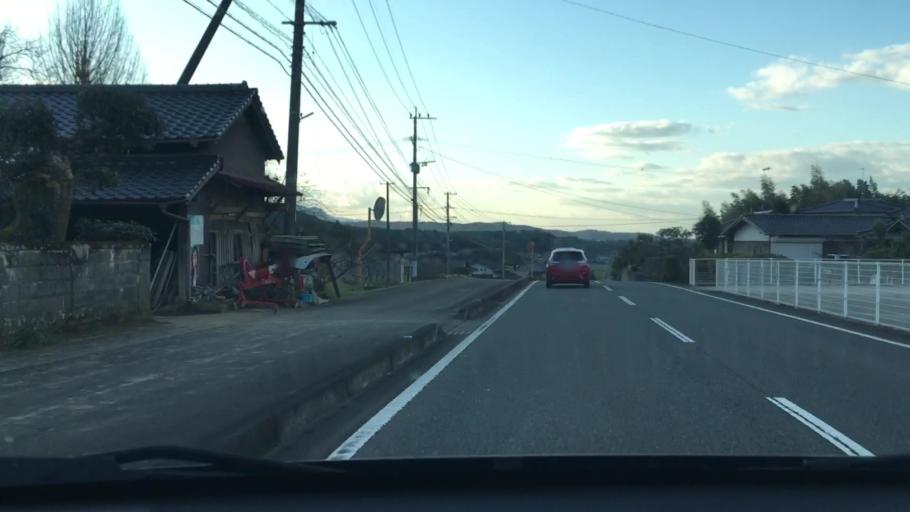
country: JP
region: Oita
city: Bungo-Takada-shi
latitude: 33.5033
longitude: 131.3683
